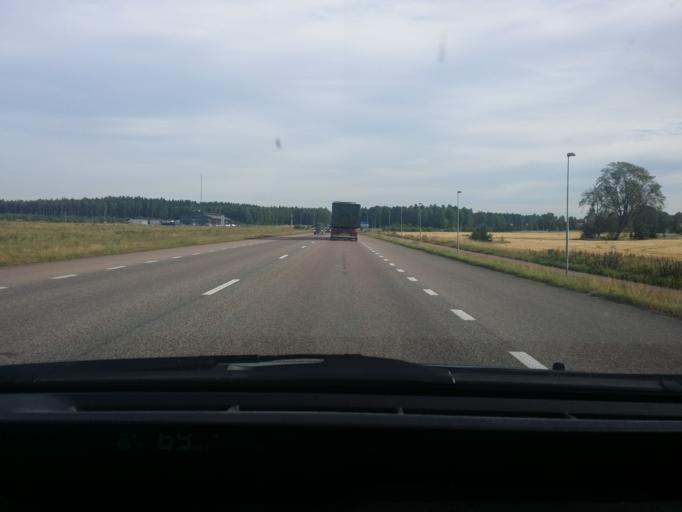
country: SE
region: Vaestmanland
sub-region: Vasteras
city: Hokasen
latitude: 59.6520
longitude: 16.5762
